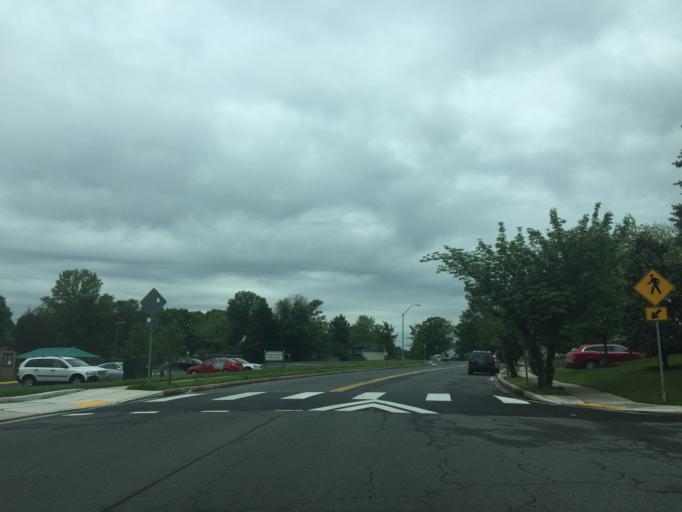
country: US
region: Maryland
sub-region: Baltimore County
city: Perry Hall
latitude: 39.3838
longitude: -76.4620
